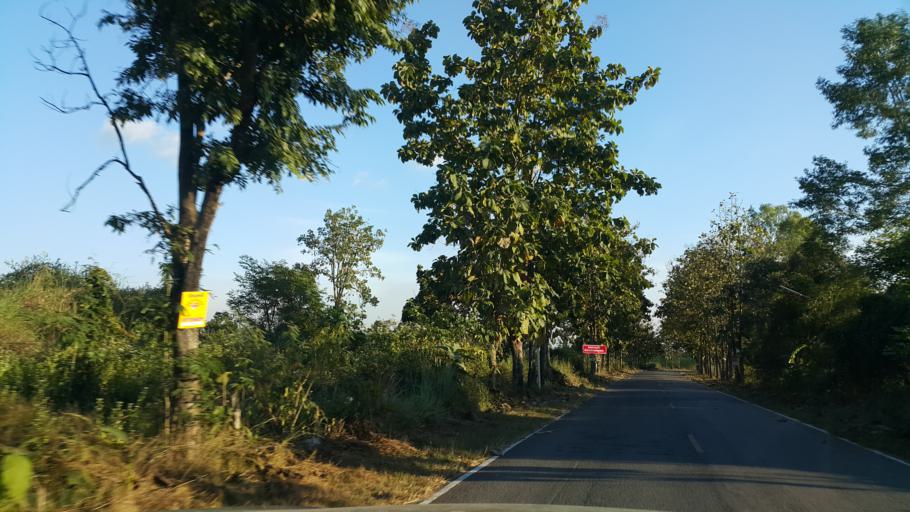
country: TH
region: Sukhothai
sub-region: Amphoe Si Satchanalai
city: Si Satchanalai
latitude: 17.5504
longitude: 99.9030
